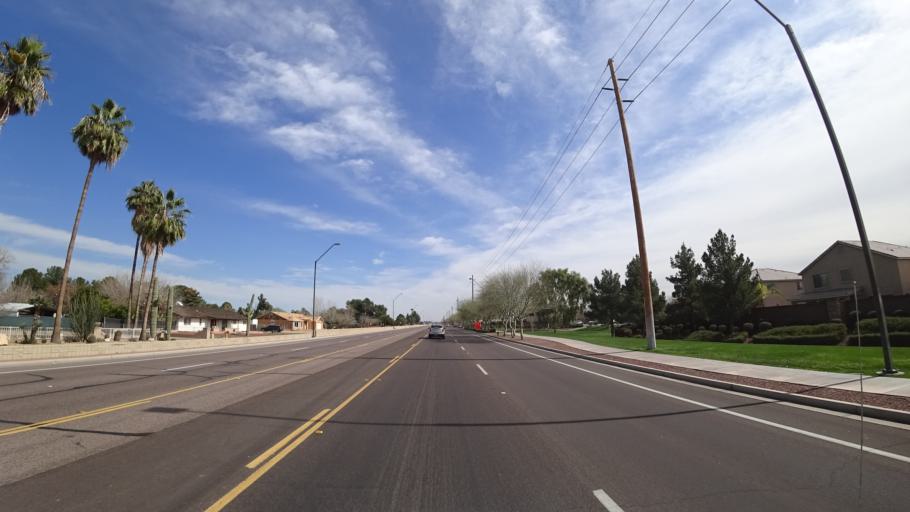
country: US
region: Arizona
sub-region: Maricopa County
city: Tolleson
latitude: 33.4789
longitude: -112.2882
